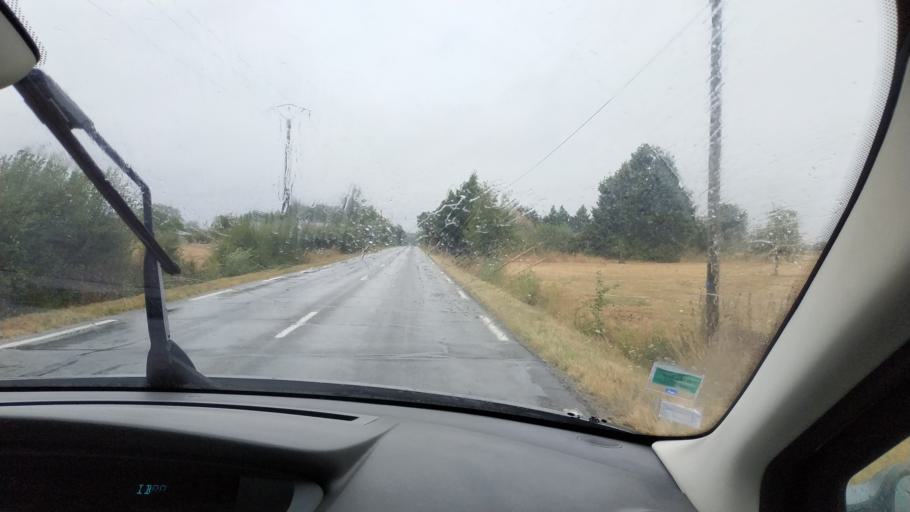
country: FR
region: Centre
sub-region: Departement du Loiret
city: Bellegarde
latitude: 47.9441
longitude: 2.3824
